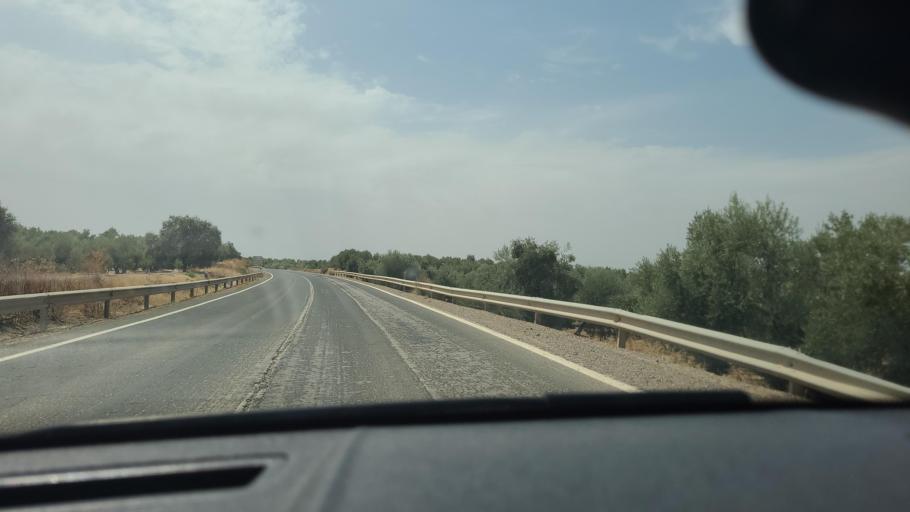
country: ES
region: Andalusia
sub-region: Provincia de Jaen
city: Jabalquinto
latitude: 38.0456
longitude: -3.7298
